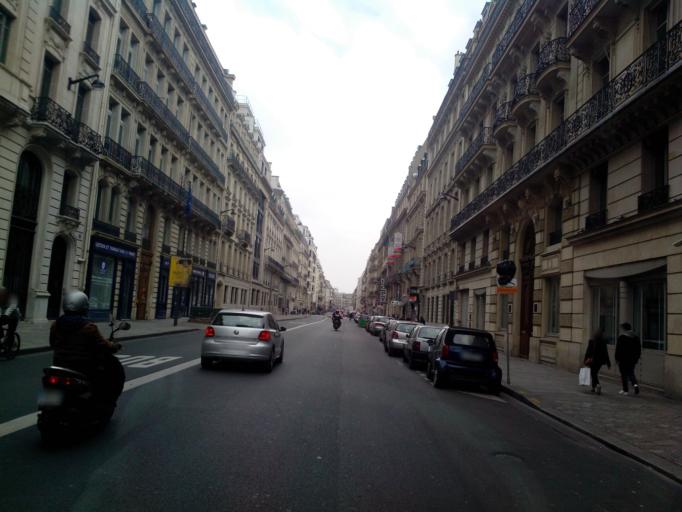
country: FR
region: Ile-de-France
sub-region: Paris
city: Saint-Ouen
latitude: 48.8763
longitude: 2.3335
